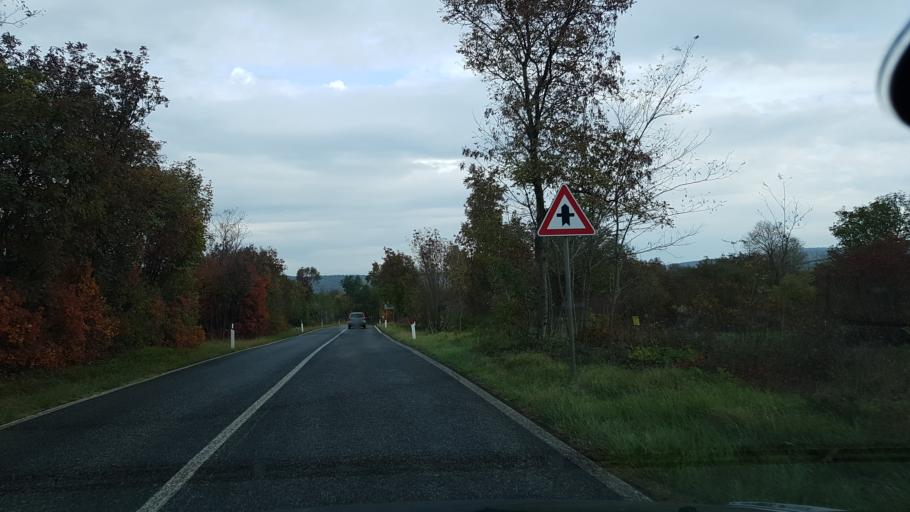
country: IT
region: Friuli Venezia Giulia
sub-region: Provincia di Gorizia
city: Doberdo del Lago
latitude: 45.8566
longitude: 13.5480
